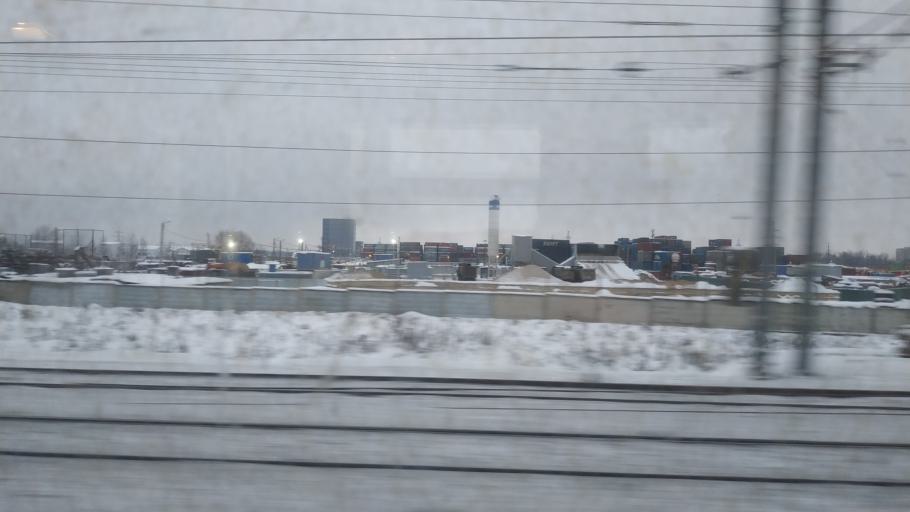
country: RU
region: Moskovskaya
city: Shcherbinka
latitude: 55.4900
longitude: 37.5563
